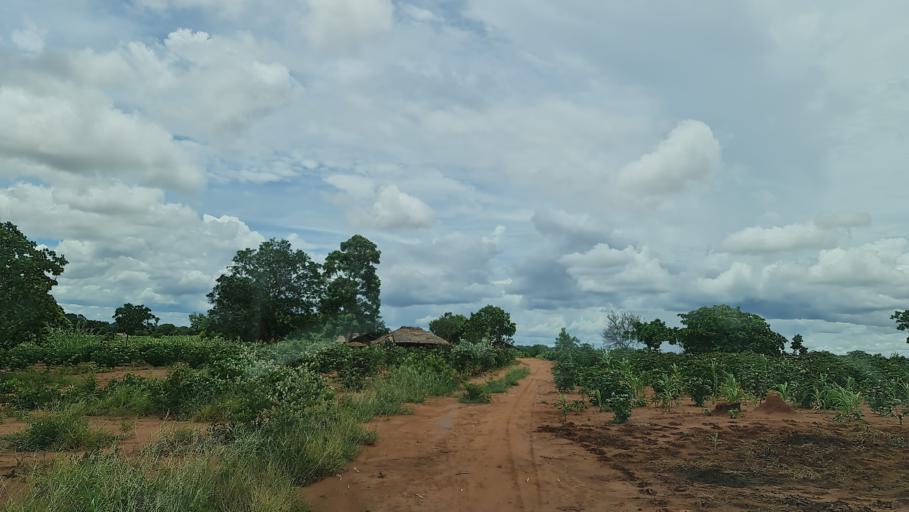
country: MZ
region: Nampula
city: Nacala
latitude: -14.7857
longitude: 39.9798
